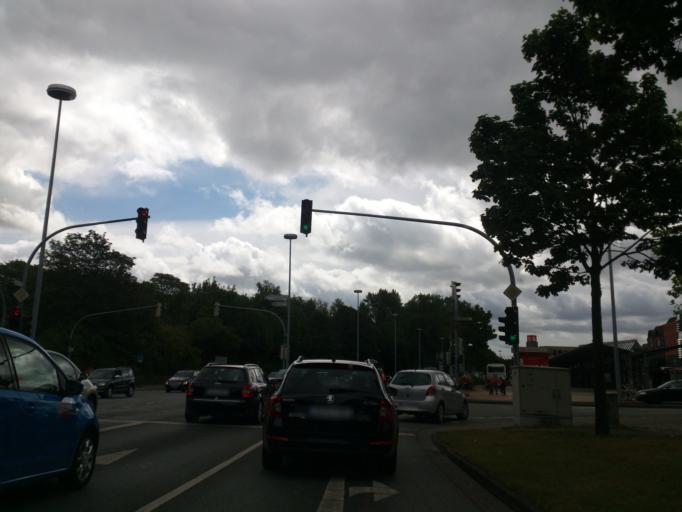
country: DE
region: Schleswig-Holstein
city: Flensburg
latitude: 54.7871
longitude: 9.4370
